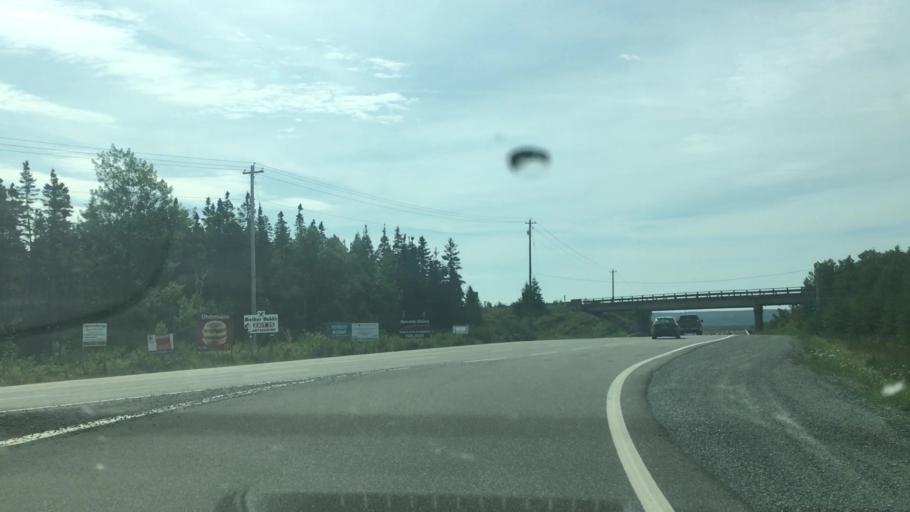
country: CA
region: Nova Scotia
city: Port Hawkesbury
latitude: 45.6264
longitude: -61.3322
